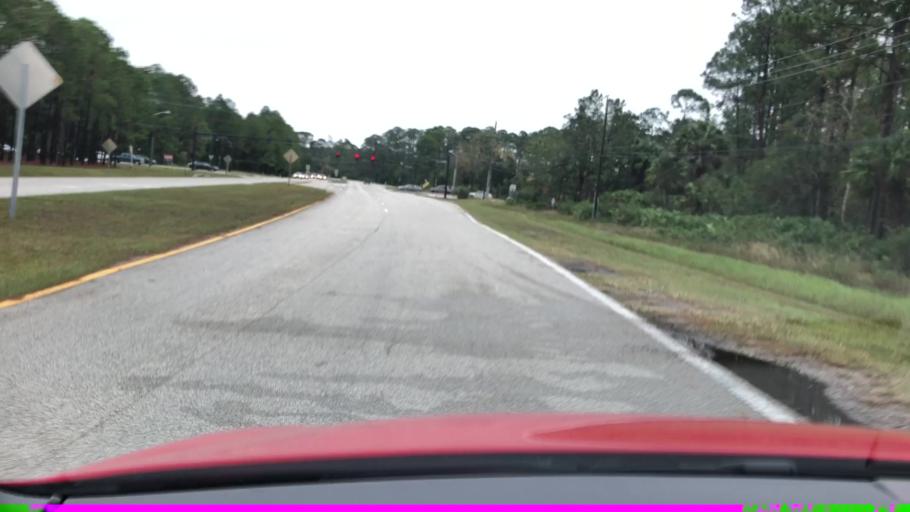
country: US
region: Florida
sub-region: Volusia County
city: Holly Hill
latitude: 29.2095
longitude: -81.0758
